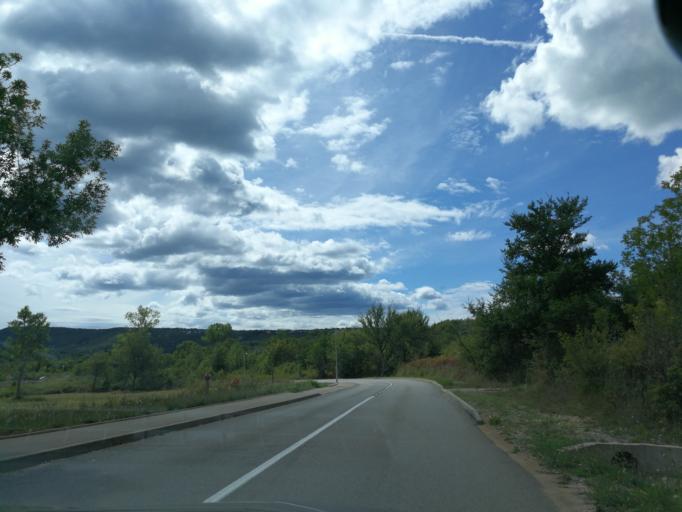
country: HR
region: Primorsko-Goranska
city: Njivice
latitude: 45.1537
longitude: 14.5971
